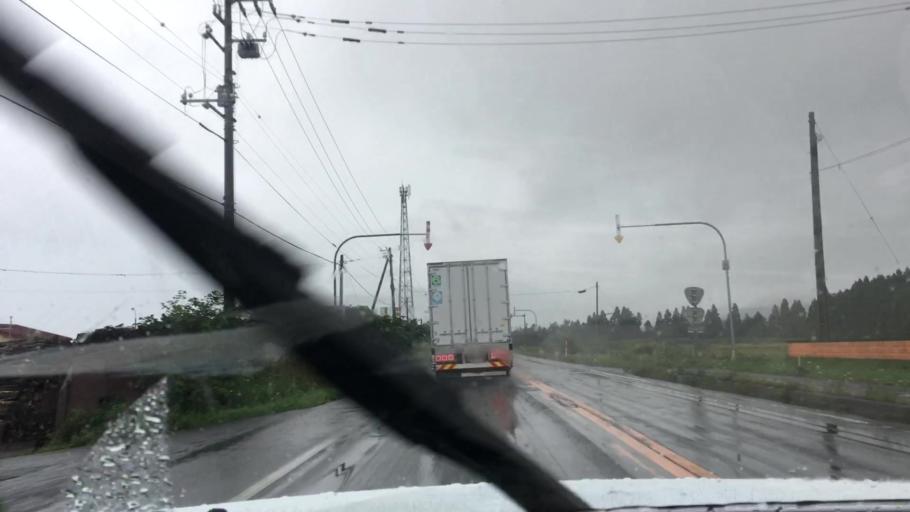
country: JP
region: Hokkaido
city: Niseko Town
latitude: 42.4741
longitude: 140.3459
